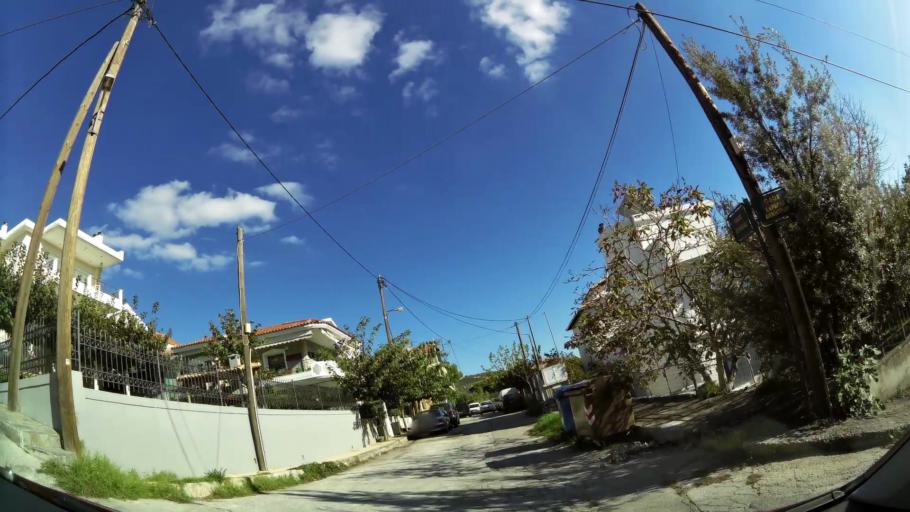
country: GR
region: Attica
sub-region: Nomarchia Athinas
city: Penteli
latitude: 38.0445
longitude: 23.8820
